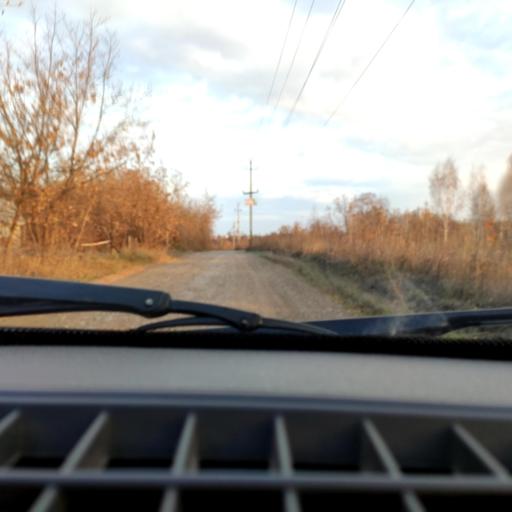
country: RU
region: Bashkortostan
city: Avdon
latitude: 54.6264
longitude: 55.7366
